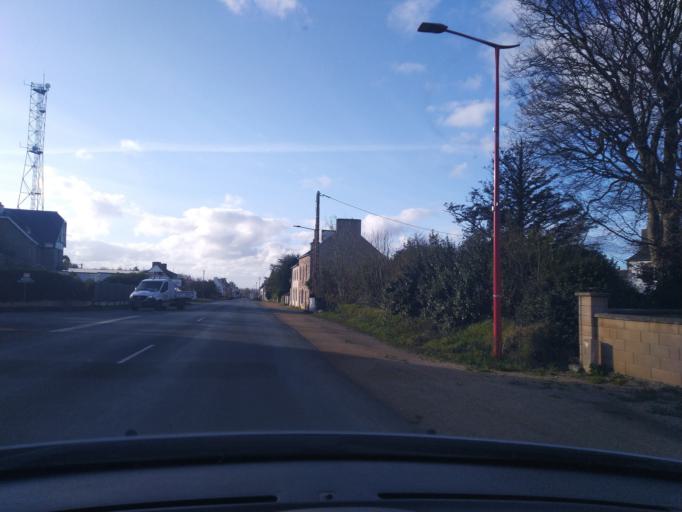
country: FR
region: Brittany
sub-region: Departement du Finistere
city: Plouigneau
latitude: 48.5691
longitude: -3.6983
